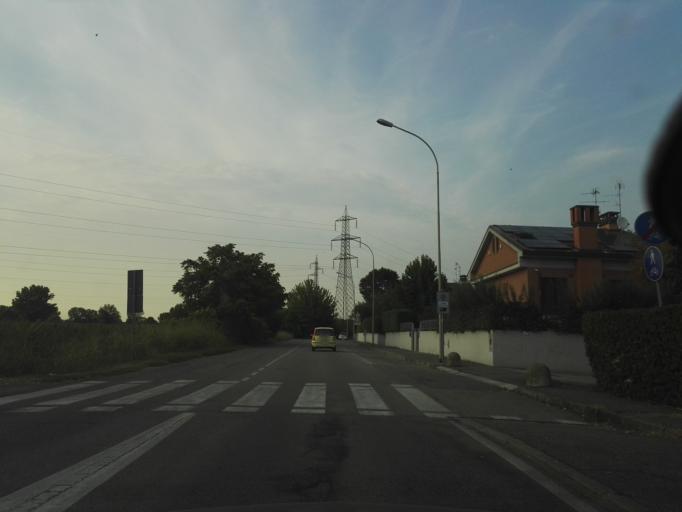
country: IT
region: Lombardy
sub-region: Citta metropolitana di Milano
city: Bettola-Zeloforomagno
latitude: 45.4334
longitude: 9.3071
